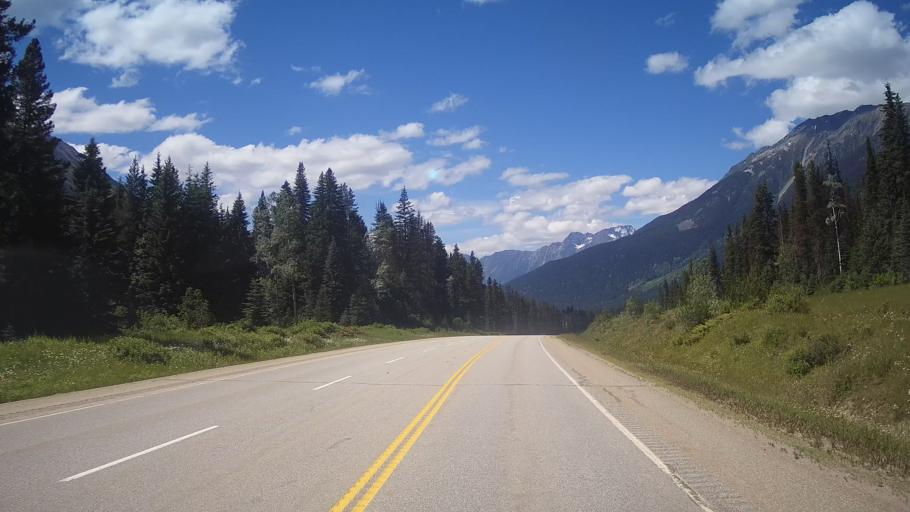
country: CA
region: Alberta
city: Grande Cache
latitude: 53.0038
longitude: -119.0471
